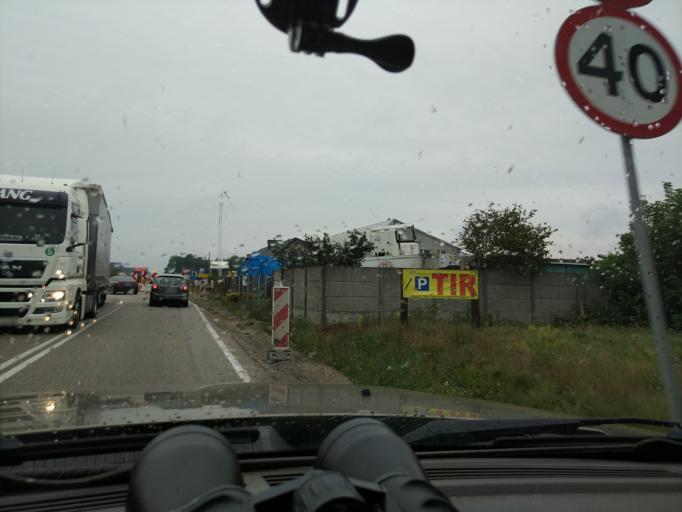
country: PL
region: Masovian Voivodeship
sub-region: Powiat ostrowski
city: Brok
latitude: 52.7601
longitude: 21.8036
